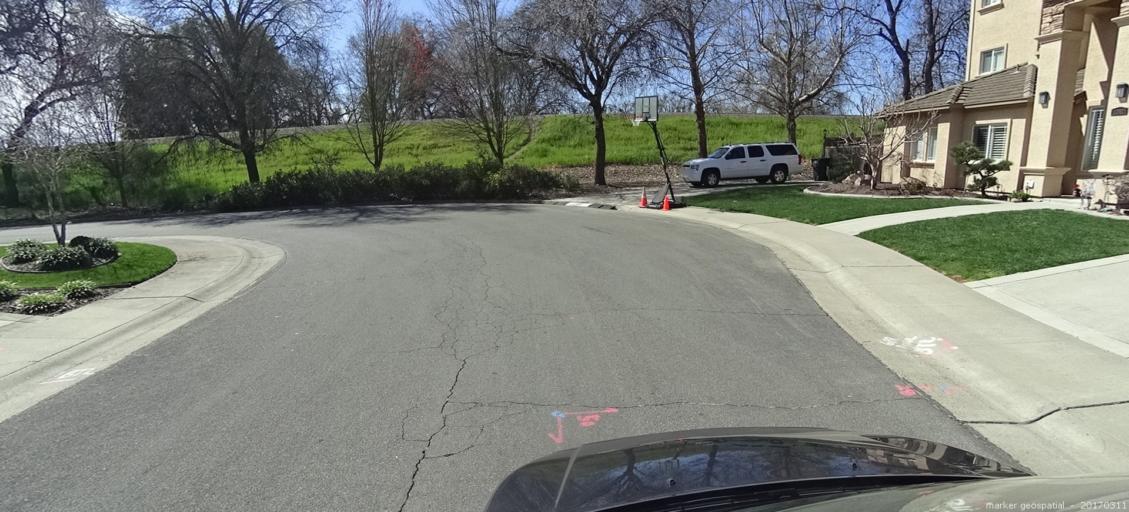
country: US
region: California
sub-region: Sacramento County
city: Parkway
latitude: 38.4818
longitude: -121.5453
